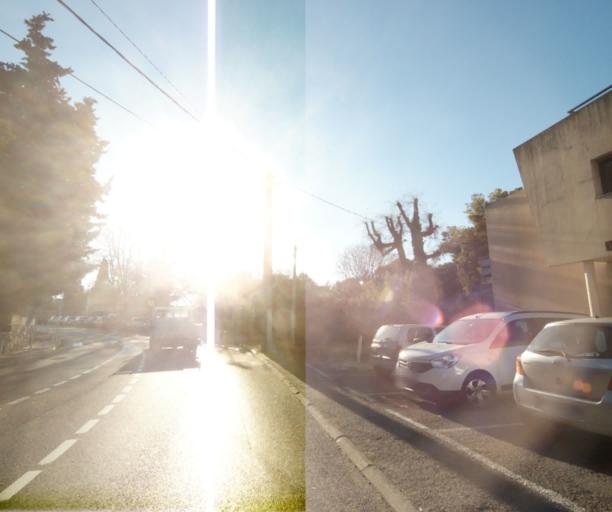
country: FR
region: Provence-Alpes-Cote d'Azur
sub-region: Departement des Alpes-Maritimes
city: Antibes
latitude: 43.5807
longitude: 7.1103
